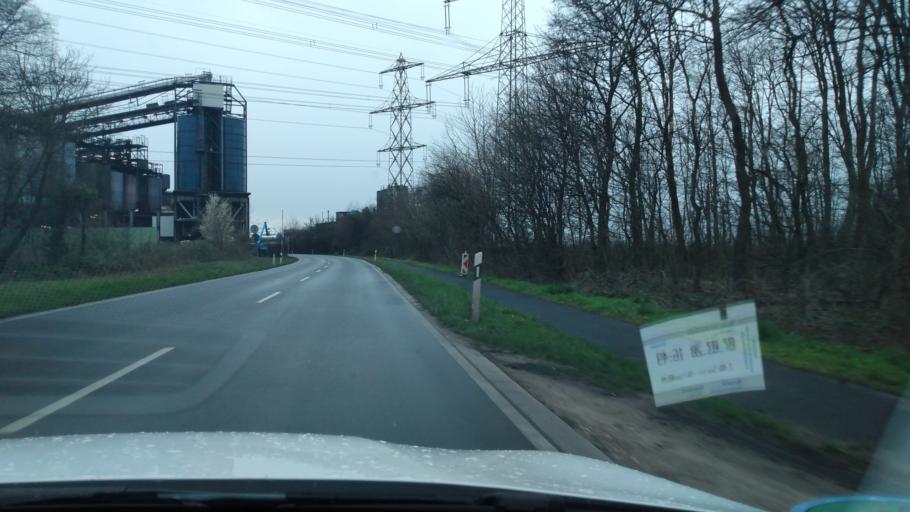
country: DE
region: North Rhine-Westphalia
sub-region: Regierungsbezirk Koln
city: Neustadt/Sued
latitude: 50.8773
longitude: 6.9264
